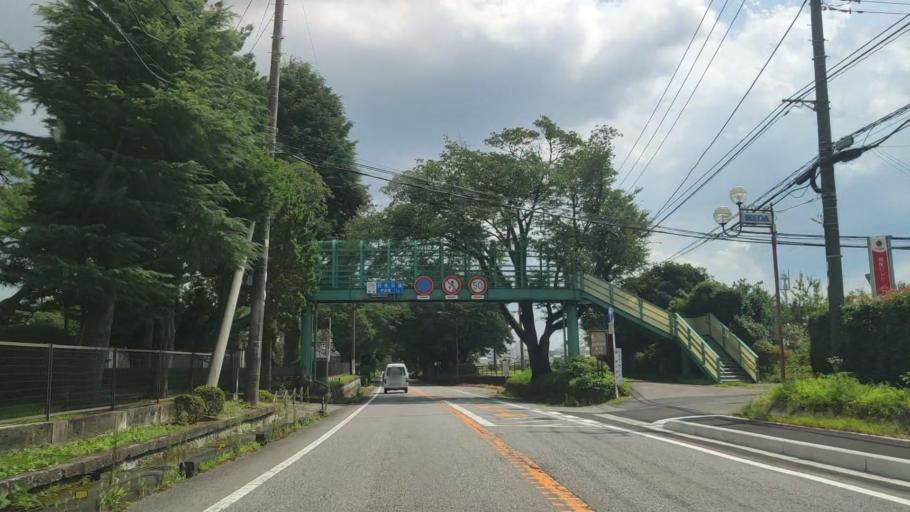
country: JP
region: Tochigi
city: Utsunomiya-shi
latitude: 36.6446
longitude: 139.8468
